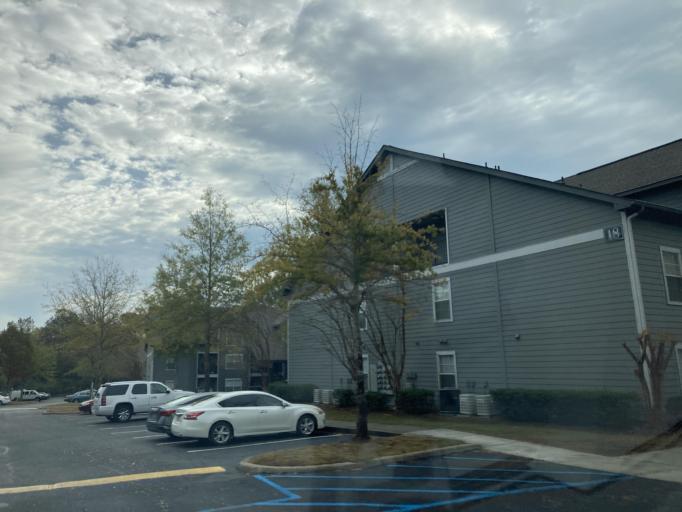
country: US
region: Mississippi
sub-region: Lamar County
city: West Hattiesburg
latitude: 31.3016
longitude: -89.3751
